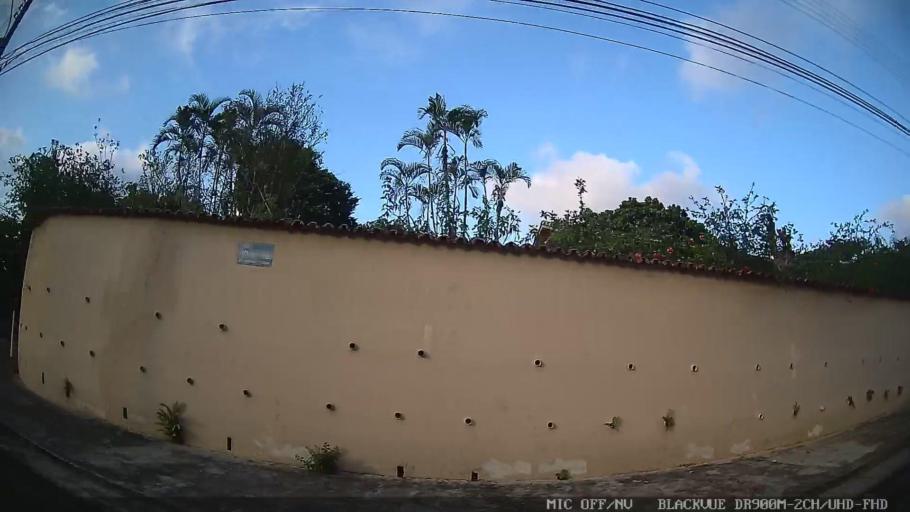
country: BR
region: Sao Paulo
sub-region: Peruibe
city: Peruibe
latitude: -24.3171
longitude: -46.9992
